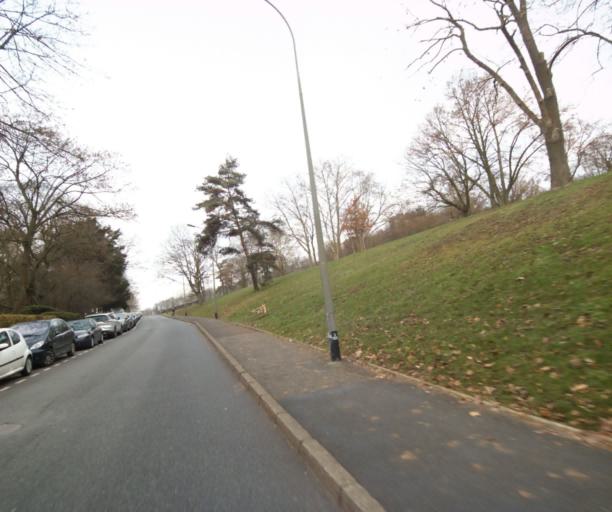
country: FR
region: Ile-de-France
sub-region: Departement des Hauts-de-Seine
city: Suresnes
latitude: 48.8707
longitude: 2.2169
